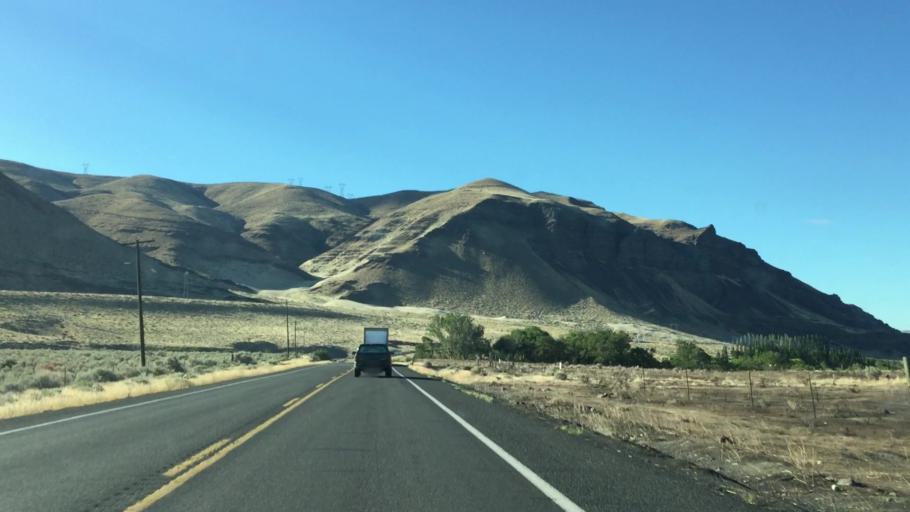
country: US
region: Washington
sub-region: Grant County
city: Mattawa
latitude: 46.8193
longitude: -119.9238
